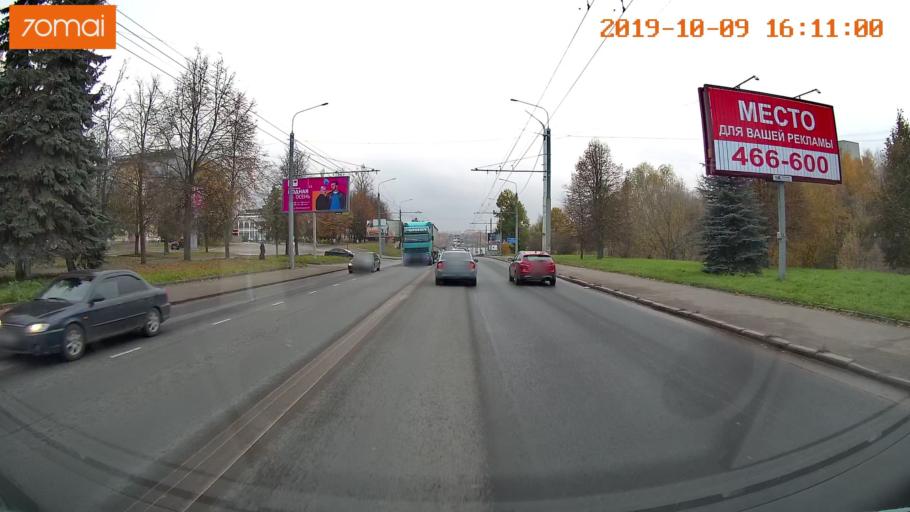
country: RU
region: Kostroma
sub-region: Kostromskoy Rayon
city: Kostroma
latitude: 57.7595
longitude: 40.9491
